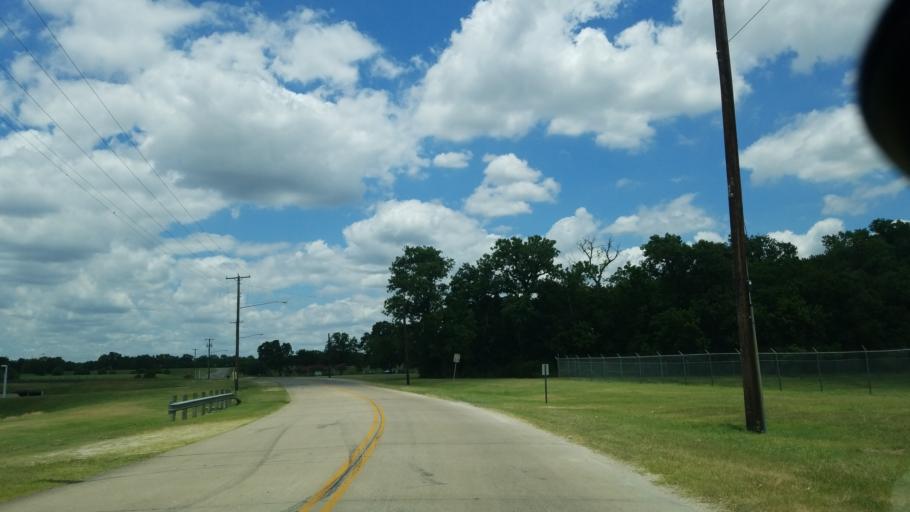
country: US
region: Texas
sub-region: Dallas County
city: Dallas
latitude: 32.7402
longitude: -96.7453
